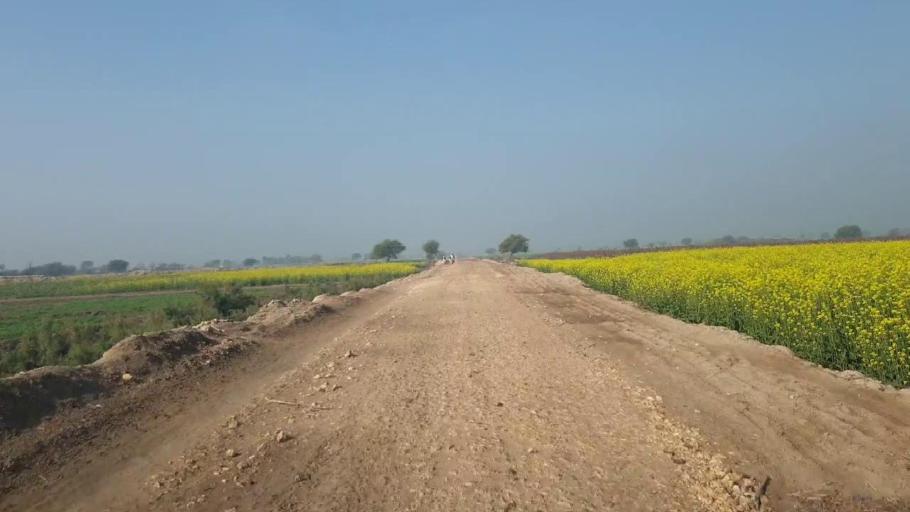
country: PK
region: Sindh
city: Shahdadpur
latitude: 25.9510
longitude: 68.5700
